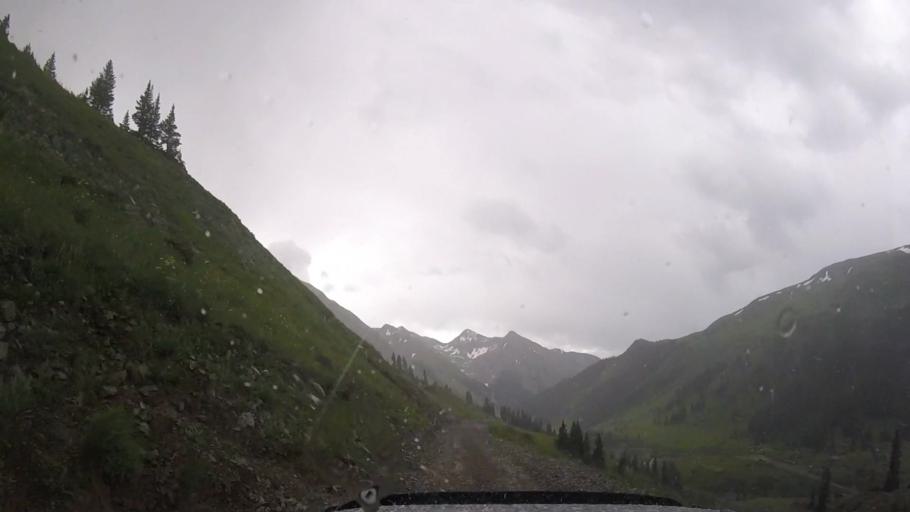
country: US
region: Colorado
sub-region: Ouray County
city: Ouray
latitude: 37.9350
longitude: -107.5695
